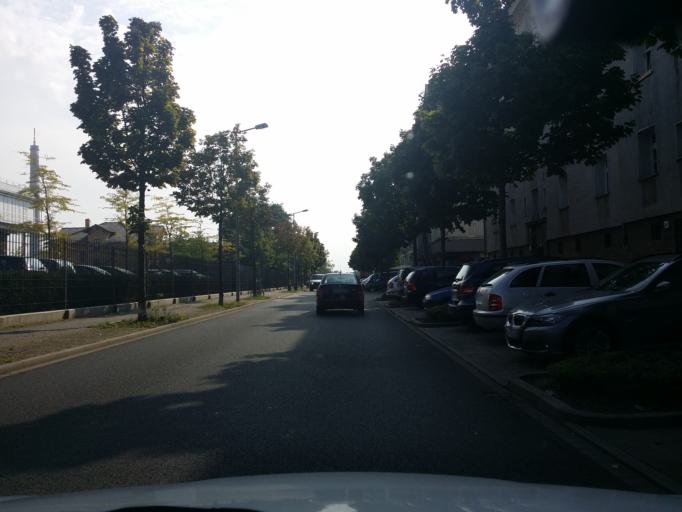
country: DE
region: Saxony
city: Leipzig
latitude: 51.3171
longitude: 12.3829
